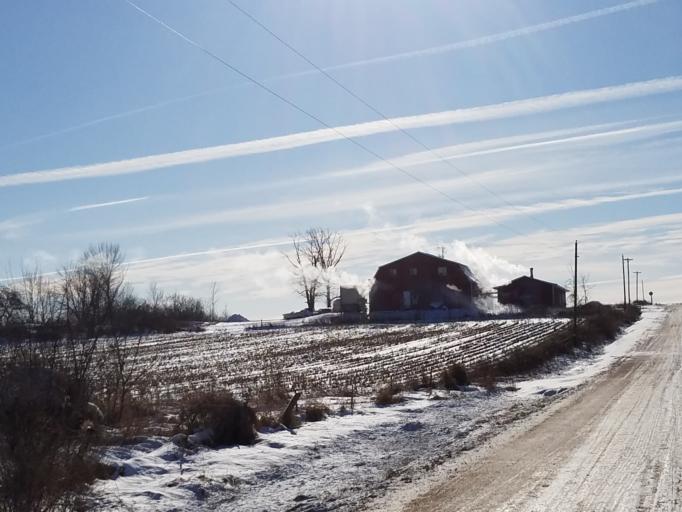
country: US
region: Wisconsin
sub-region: Clark County
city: Neillsville
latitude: 44.5845
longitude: -90.4361
